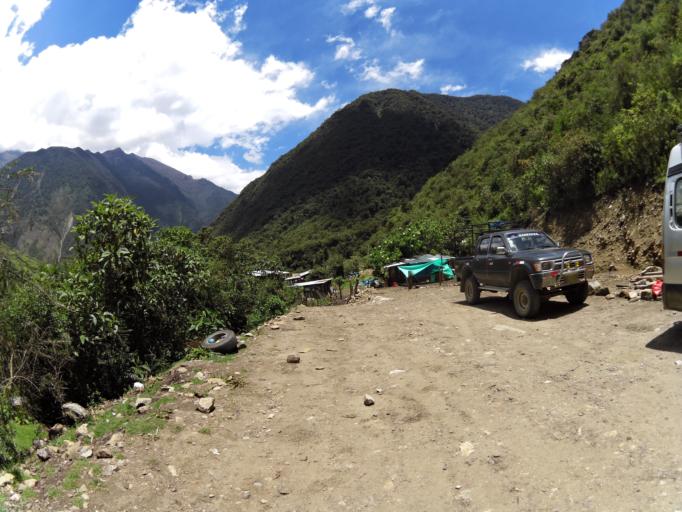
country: PE
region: Cusco
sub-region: Provincia de La Convencion
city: Santa Teresa
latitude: -13.3251
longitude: -72.6645
